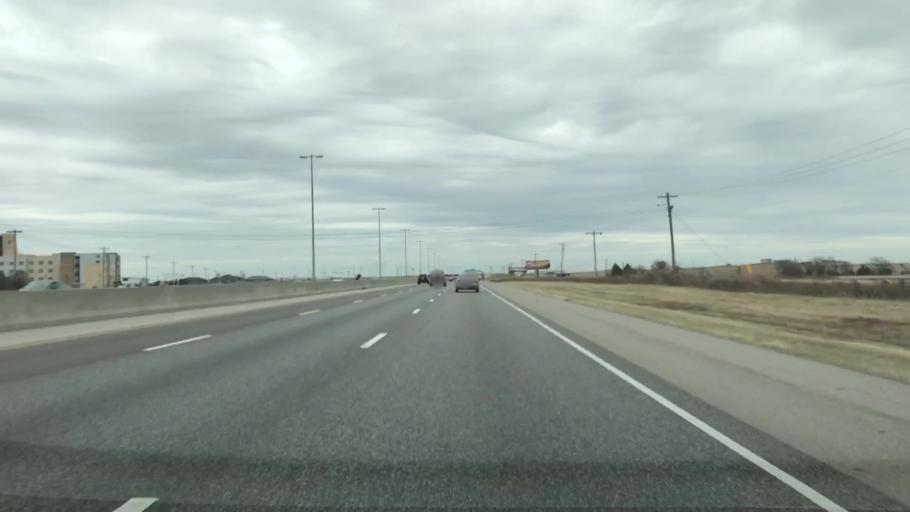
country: US
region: Oklahoma
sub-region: Cleveland County
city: Norman
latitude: 35.2539
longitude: -97.4854
